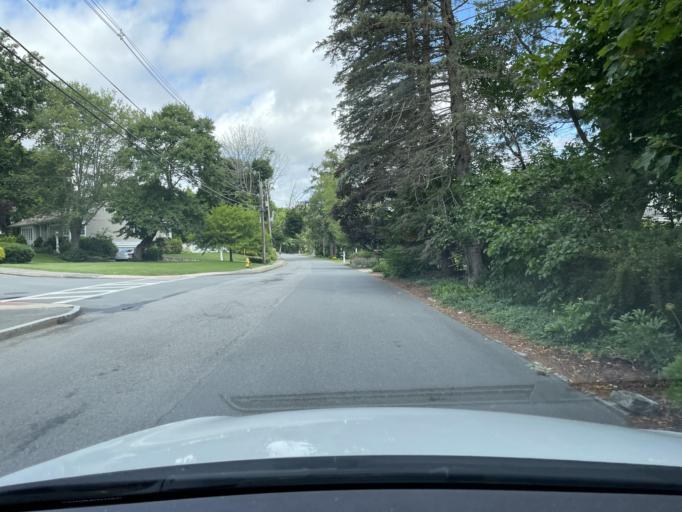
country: US
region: Massachusetts
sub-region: Essex County
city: Andover
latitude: 42.6397
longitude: -71.1235
